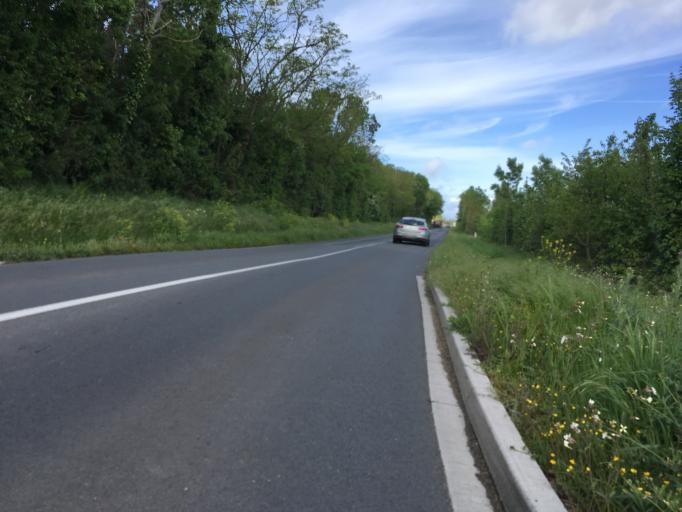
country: FR
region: Poitou-Charentes
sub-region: Departement de la Charente-Maritime
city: Dompierre-sur-Mer
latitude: 46.1719
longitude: -1.0716
